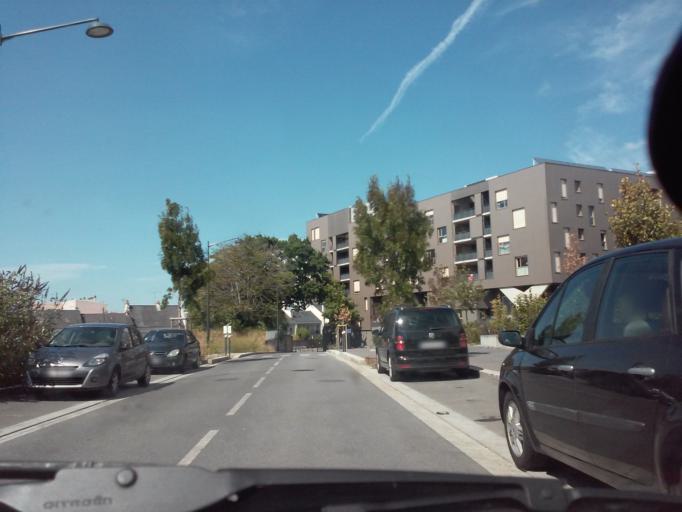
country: FR
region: Brittany
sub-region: Departement d'Ille-et-Vilaine
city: Rennes
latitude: 48.1010
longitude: -1.6987
